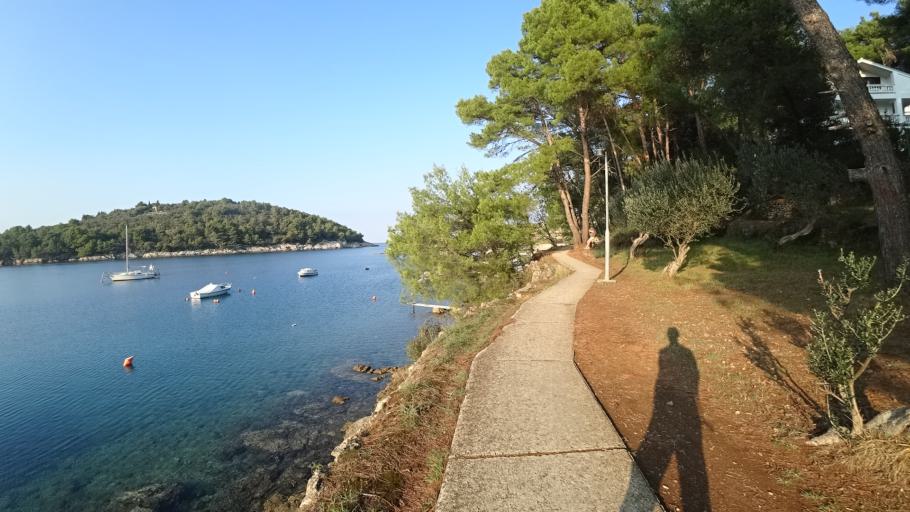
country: HR
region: Primorsko-Goranska
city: Mali Losinj
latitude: 44.5267
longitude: 14.4837
